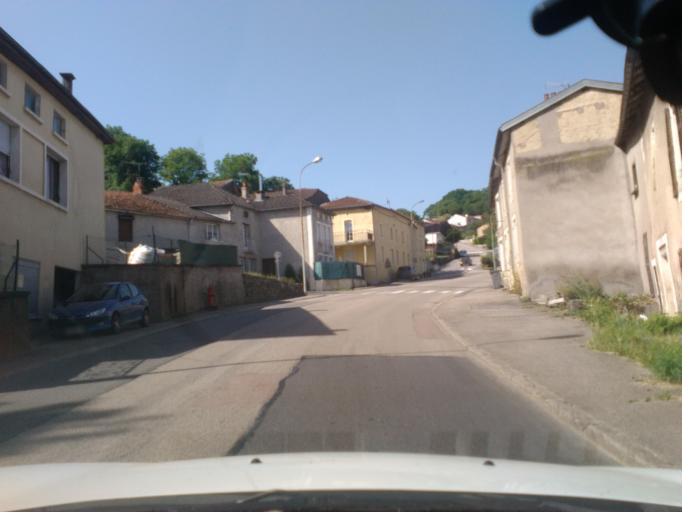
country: FR
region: Lorraine
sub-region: Departement des Vosges
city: Chatenois
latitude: 48.3016
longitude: 5.8320
